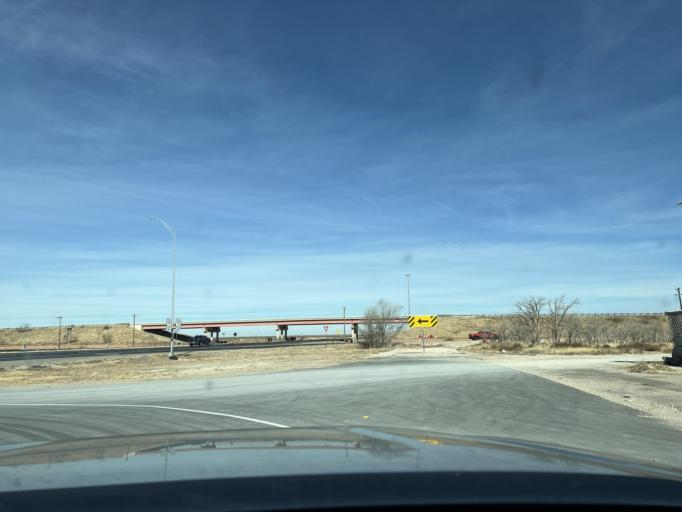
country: US
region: Texas
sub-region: Ector County
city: Gardendale
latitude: 32.0223
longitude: -102.4294
